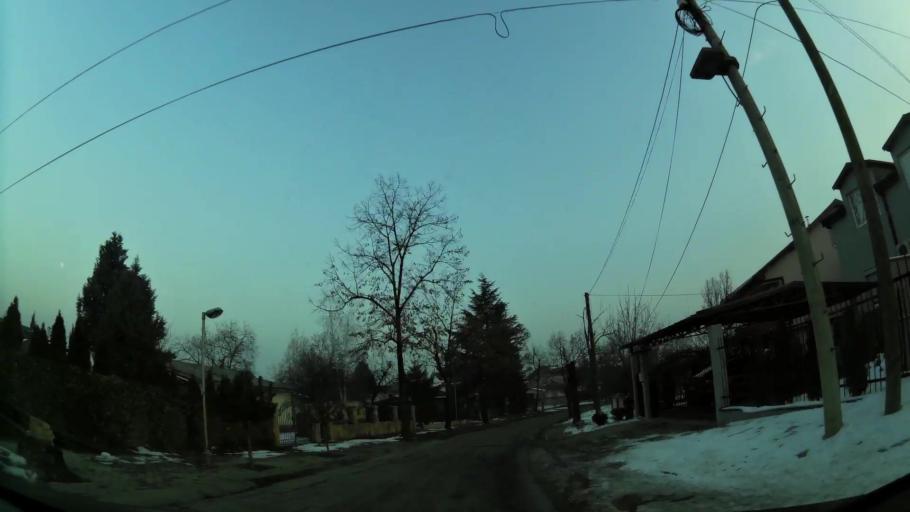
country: MK
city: Creshevo
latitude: 42.0091
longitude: 21.5101
